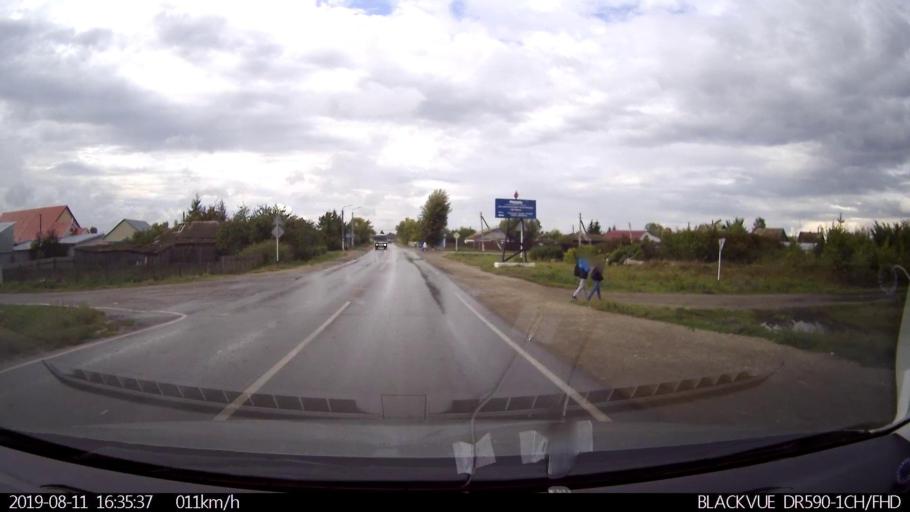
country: RU
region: Ulyanovsk
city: Mayna
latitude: 54.1153
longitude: 47.6151
